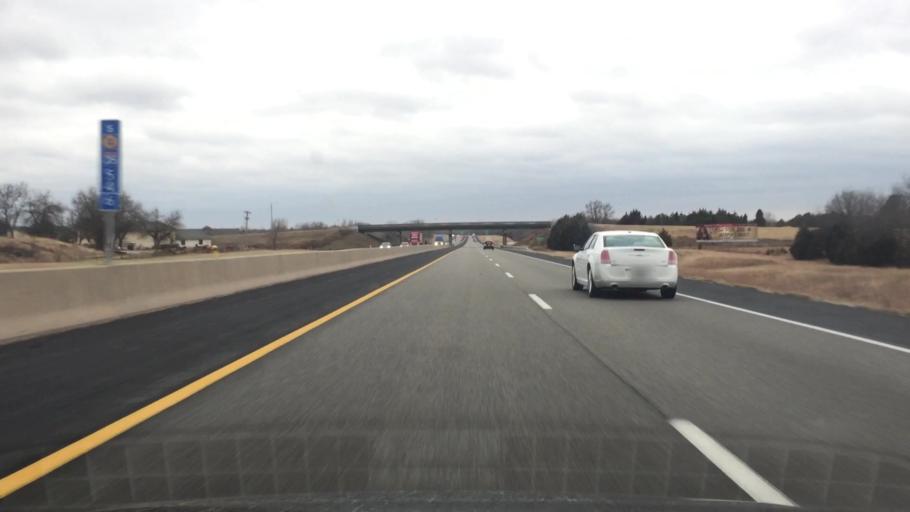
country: US
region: Kansas
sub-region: Butler County
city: Andover
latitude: 37.7028
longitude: -97.1509
